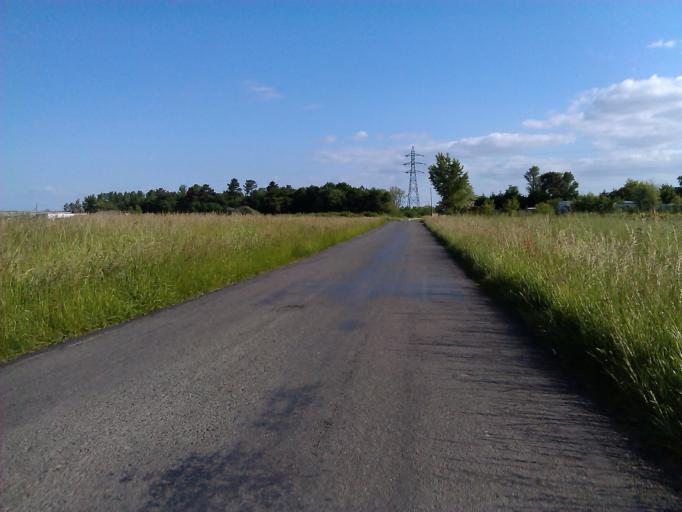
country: FR
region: Aquitaine
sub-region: Departement de la Gironde
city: Saint-Gervais
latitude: 45.0184
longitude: -0.4431
